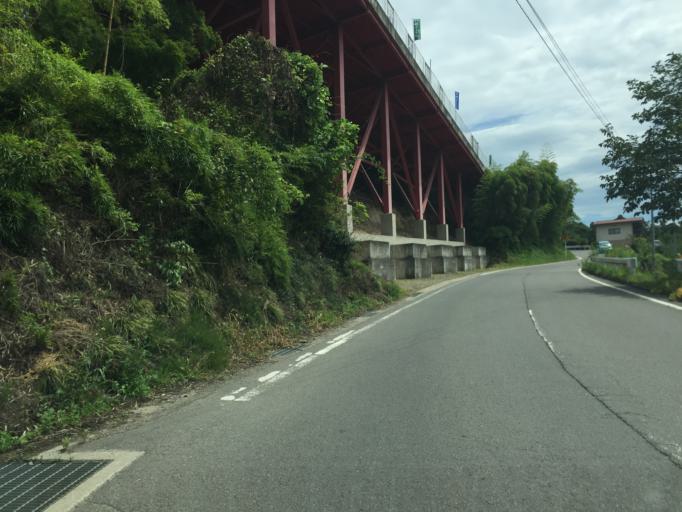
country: JP
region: Fukushima
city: Fukushima-shi
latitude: 37.8243
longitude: 140.4129
